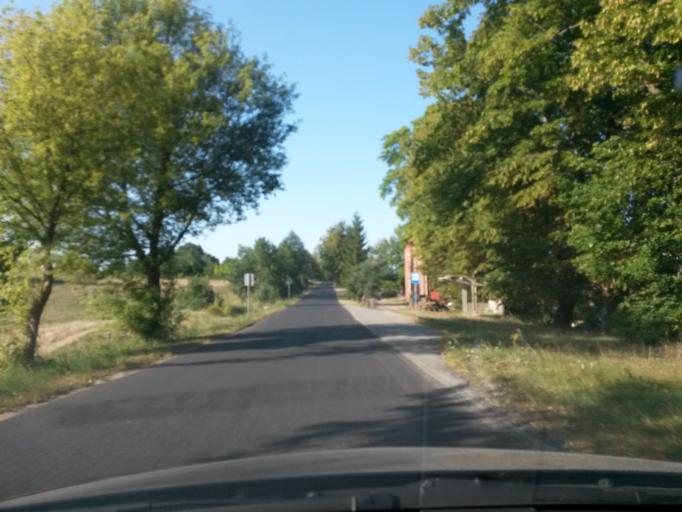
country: PL
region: Kujawsko-Pomorskie
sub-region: Powiat brodnicki
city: Gorzno
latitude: 53.1752
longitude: 19.6390
